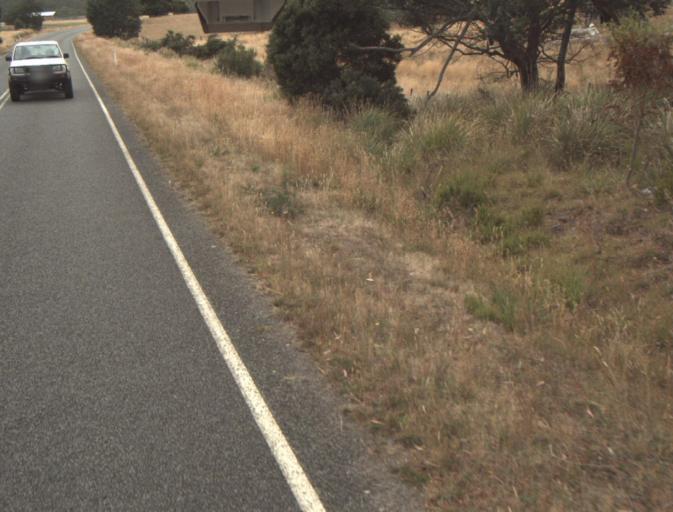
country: AU
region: Tasmania
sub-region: Northern Midlands
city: Evandale
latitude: -41.4727
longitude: 147.5454
